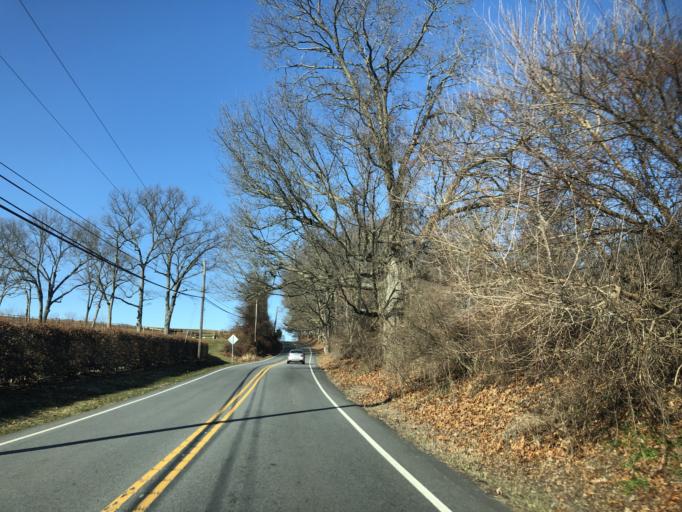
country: US
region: Pennsylvania
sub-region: Chester County
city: South Coatesville
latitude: 39.9238
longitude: -75.8253
